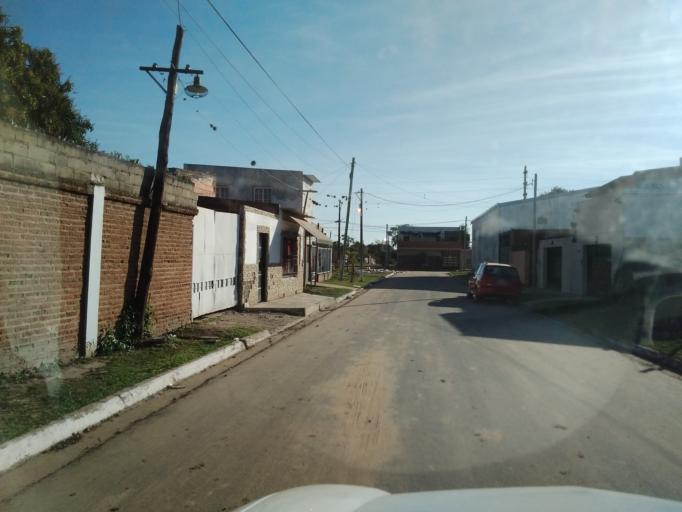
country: AR
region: Corrientes
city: Corrientes
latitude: -27.4970
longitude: -58.8405
